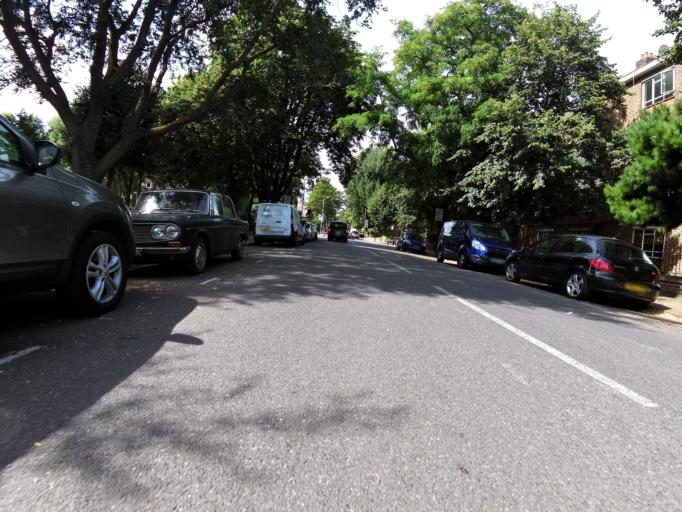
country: GB
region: England
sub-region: Greater London
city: Holloway
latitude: 51.5511
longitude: -0.1254
